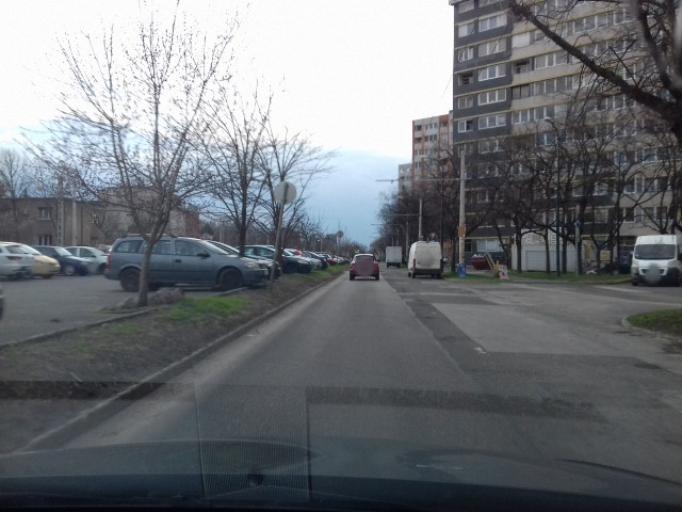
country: HU
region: Budapest
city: Budapest XVI. keruelet
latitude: 47.5107
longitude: 19.1416
